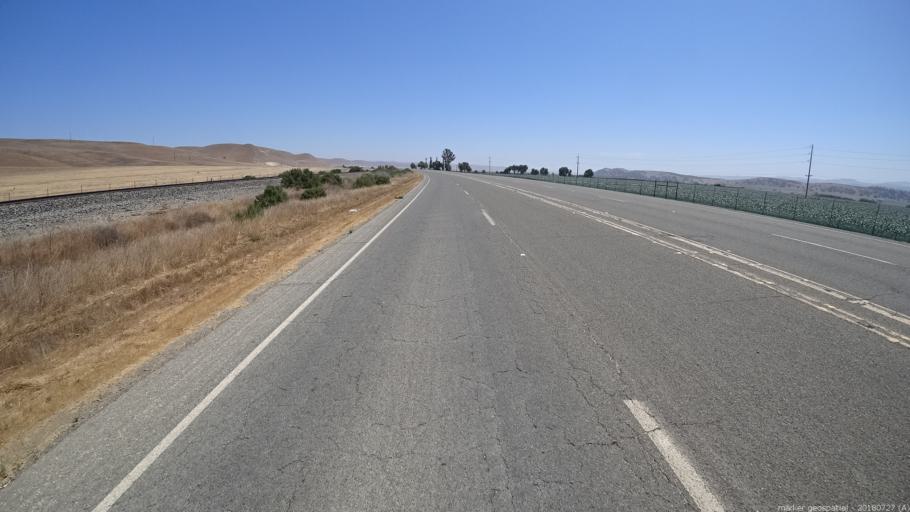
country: US
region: California
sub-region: Monterey County
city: King City
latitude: 36.1062
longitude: -120.9914
